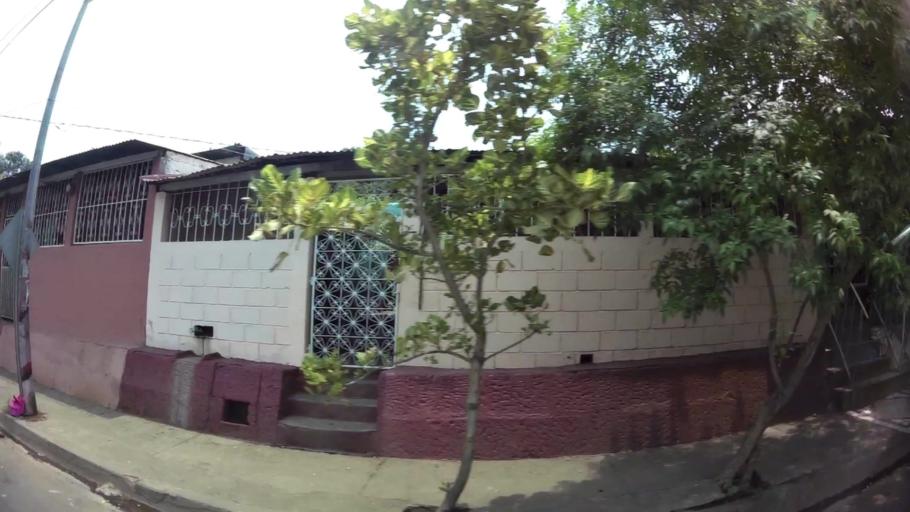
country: NI
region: Managua
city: Managua
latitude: 12.1147
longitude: -86.2977
